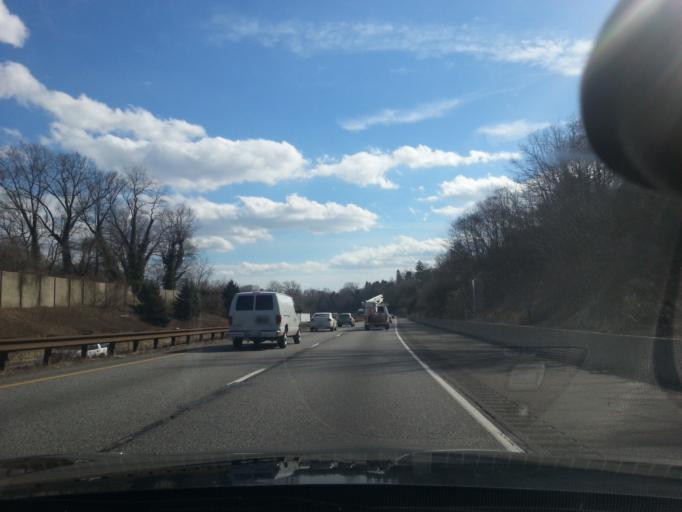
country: US
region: Pennsylvania
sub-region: Delaware County
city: Swarthmore
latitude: 39.8956
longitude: -75.3594
